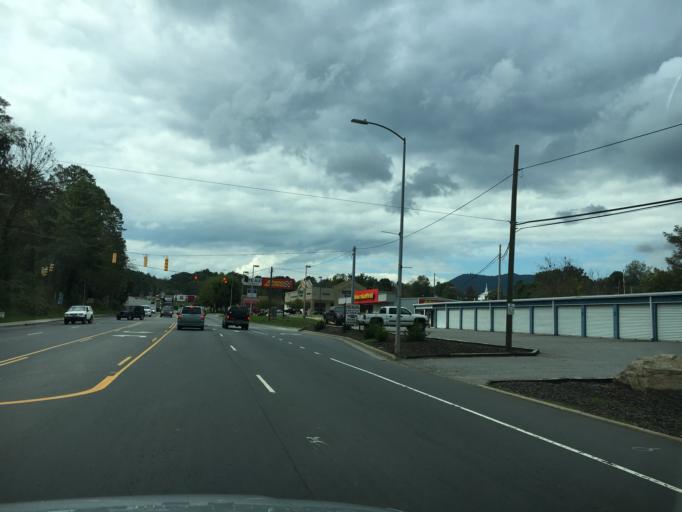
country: US
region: North Carolina
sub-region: Haywood County
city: West Canton
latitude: 35.5323
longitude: -82.8508
